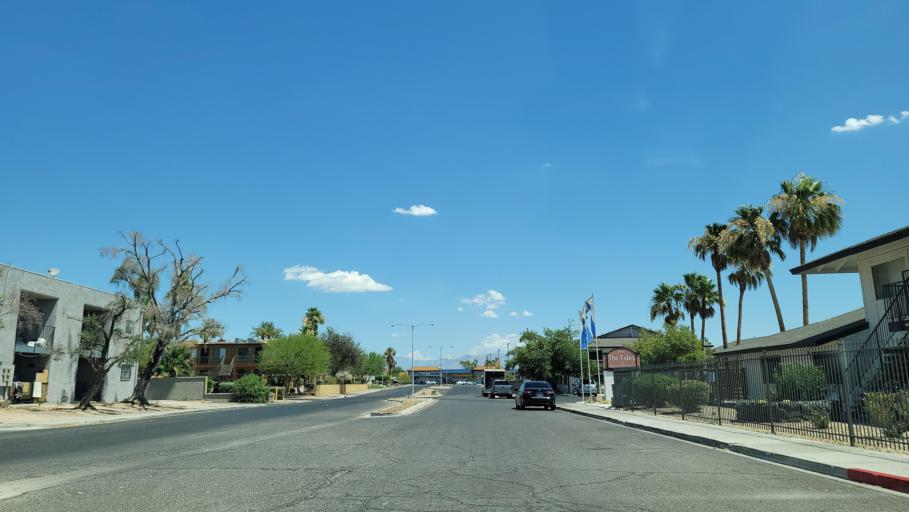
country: US
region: Nevada
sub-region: Clark County
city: Spring Valley
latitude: 36.1239
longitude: -115.2030
